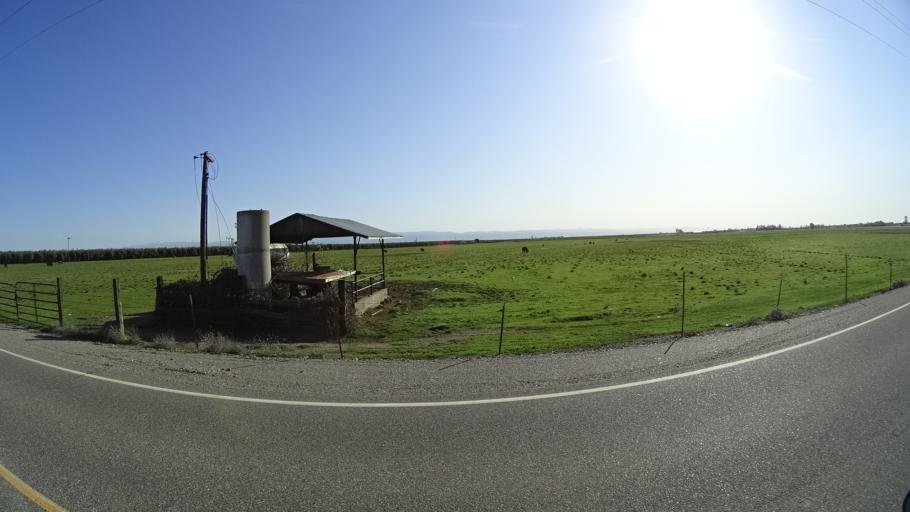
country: US
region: California
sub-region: Glenn County
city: Hamilton City
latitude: 39.7501
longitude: -122.1001
